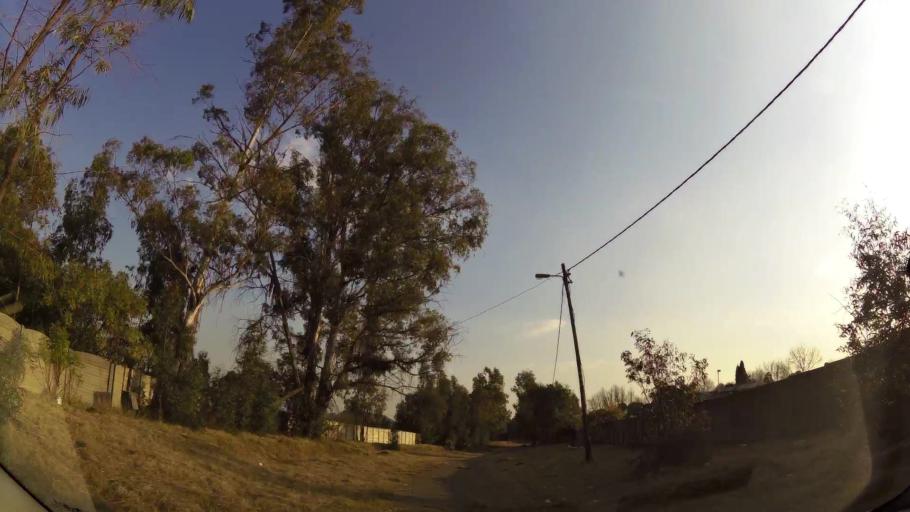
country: ZA
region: Gauteng
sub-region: Ekurhuleni Metropolitan Municipality
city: Benoni
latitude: -26.1534
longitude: 28.3689
